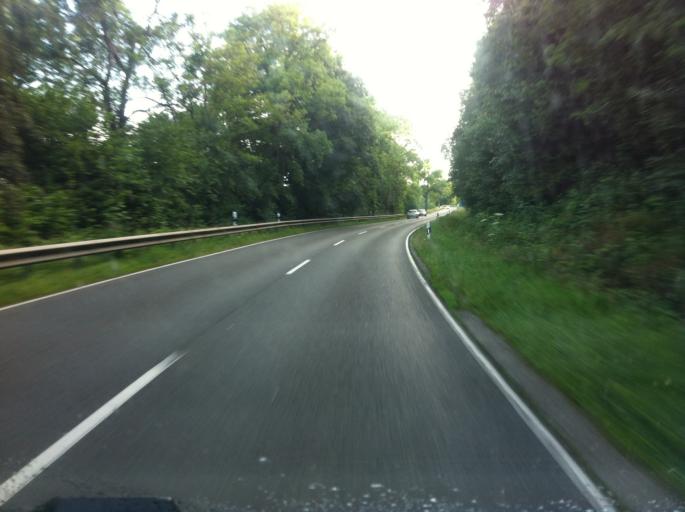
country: DE
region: North Rhine-Westphalia
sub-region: Regierungsbezirk Koln
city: Nettersheim
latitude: 50.5202
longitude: 6.6542
